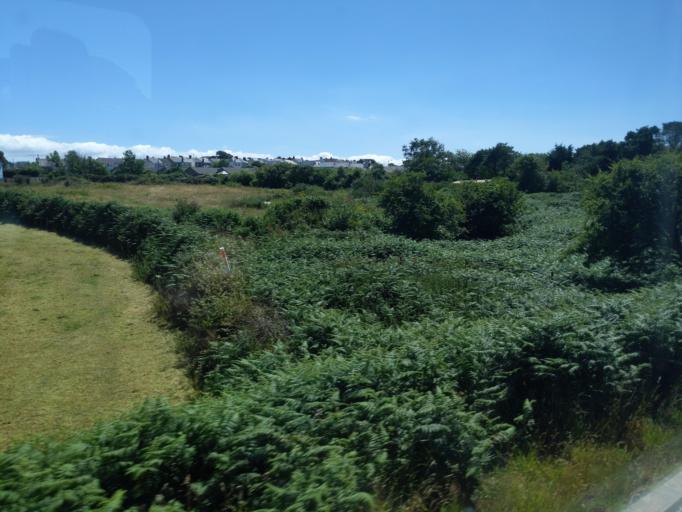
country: GB
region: England
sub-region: Cornwall
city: Redruth
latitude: 50.2490
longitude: -5.2129
